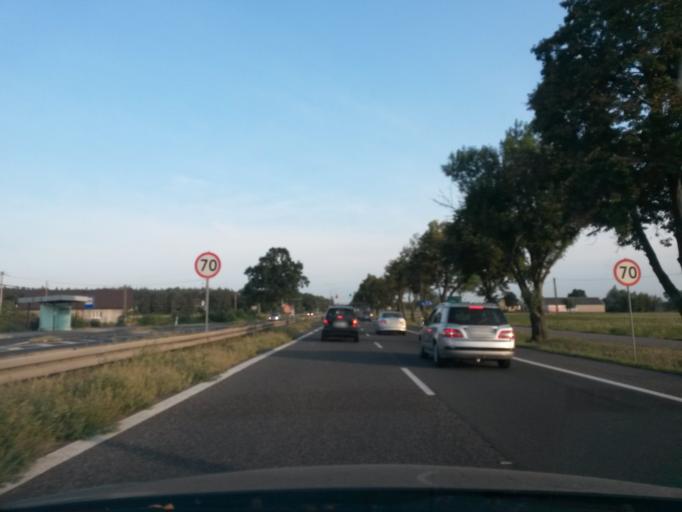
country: PL
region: Masovian Voivodeship
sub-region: Powiat nowodworski
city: Zakroczym
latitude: 52.4637
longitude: 20.5739
